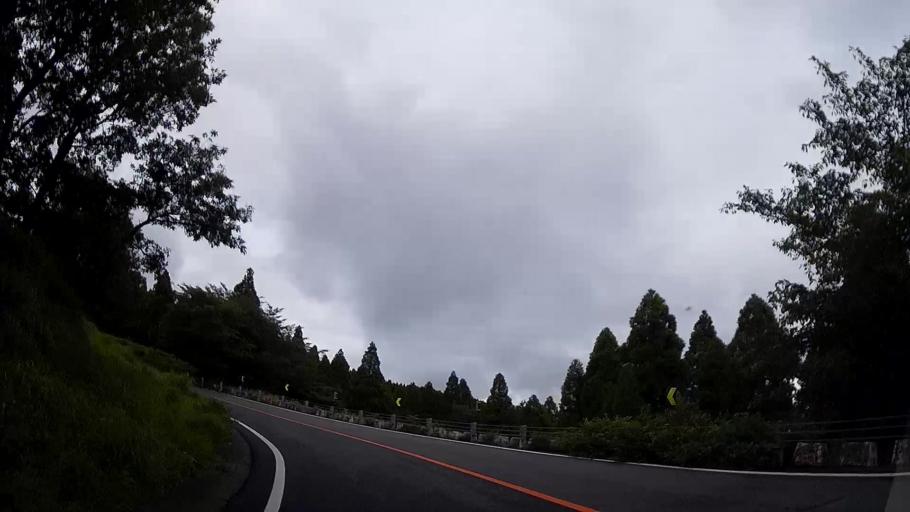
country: JP
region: Kumamoto
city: Aso
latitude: 32.8931
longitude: 131.0468
